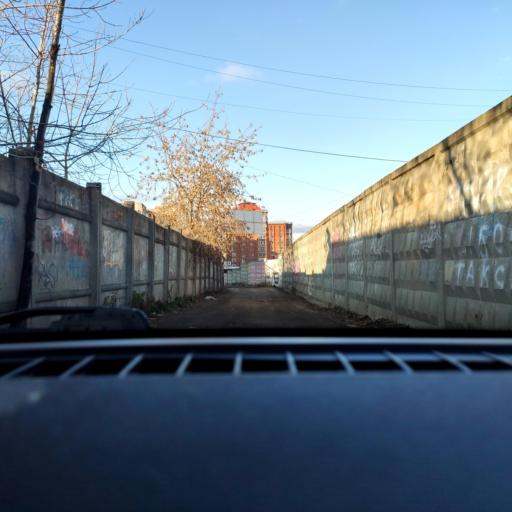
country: RU
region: Perm
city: Perm
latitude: 57.9931
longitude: 56.2122
